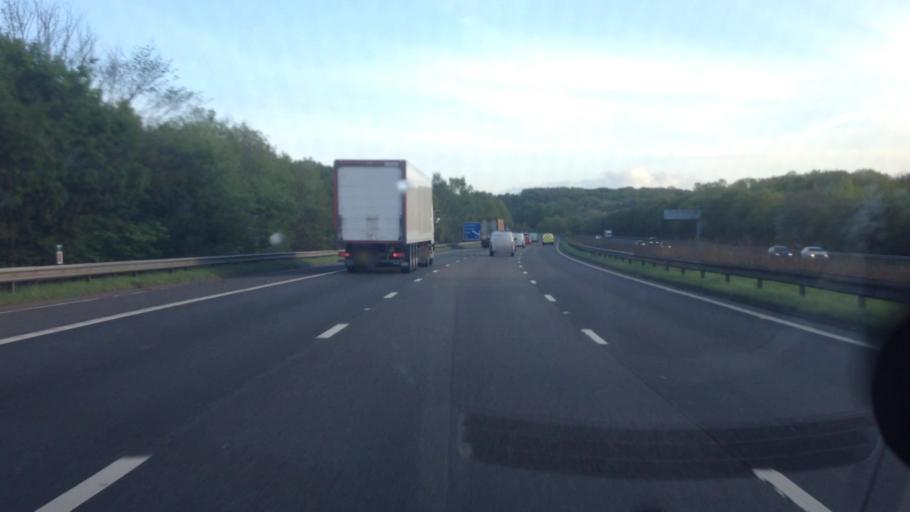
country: GB
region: England
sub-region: Barnsley
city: Birdwell
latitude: 53.5169
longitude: -1.4881
